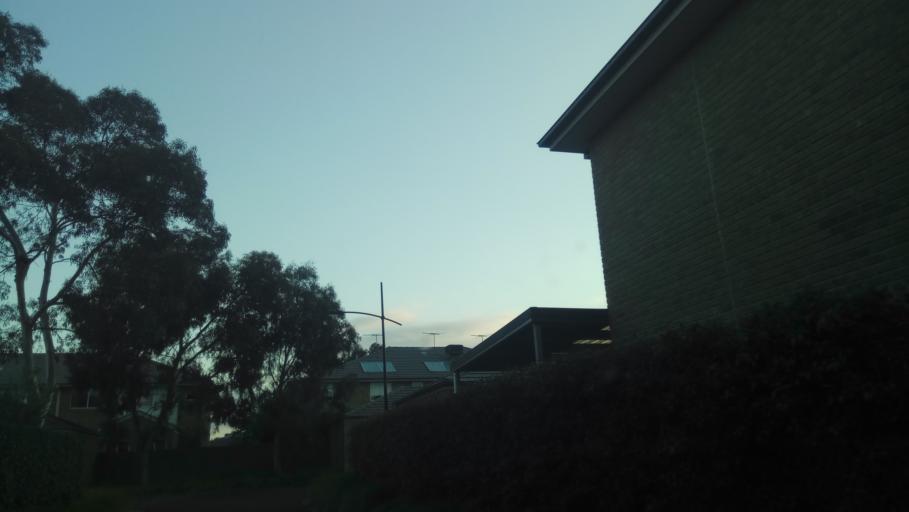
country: AU
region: Victoria
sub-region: Wyndham
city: Point Cook
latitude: -37.9053
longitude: 144.7492
